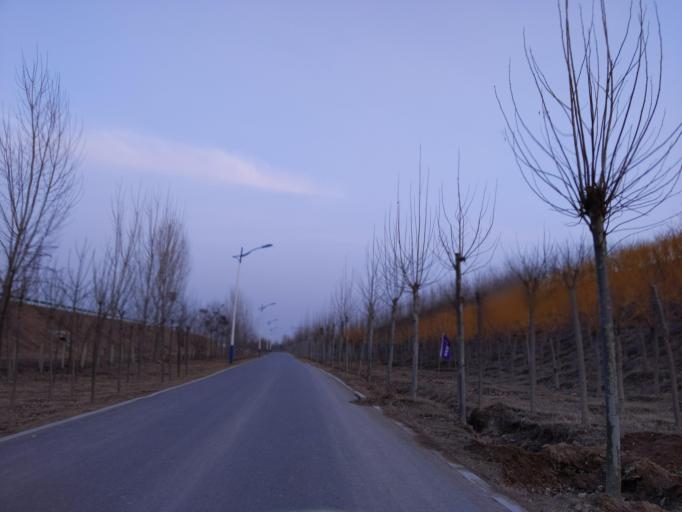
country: CN
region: Henan Sheng
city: Zhongyuanlu
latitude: 35.8147
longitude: 115.0626
